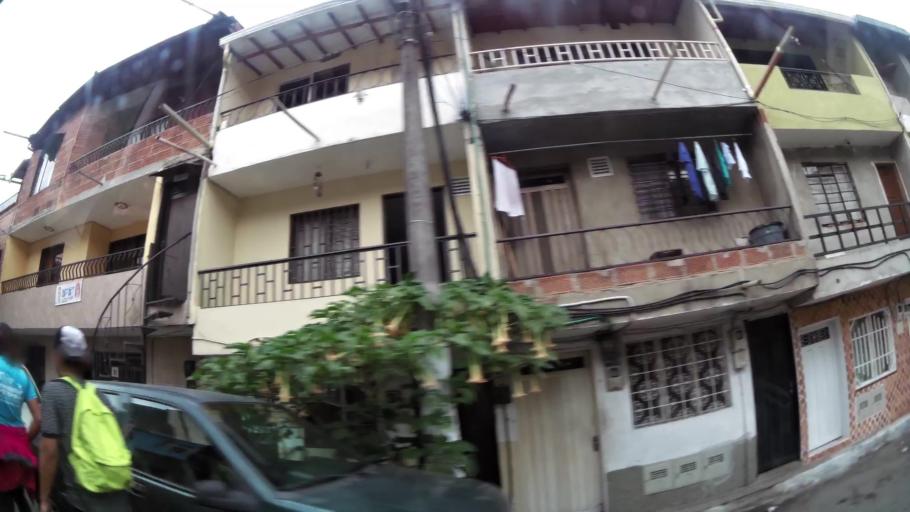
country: CO
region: Antioquia
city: Bello
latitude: 6.3089
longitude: -75.5548
